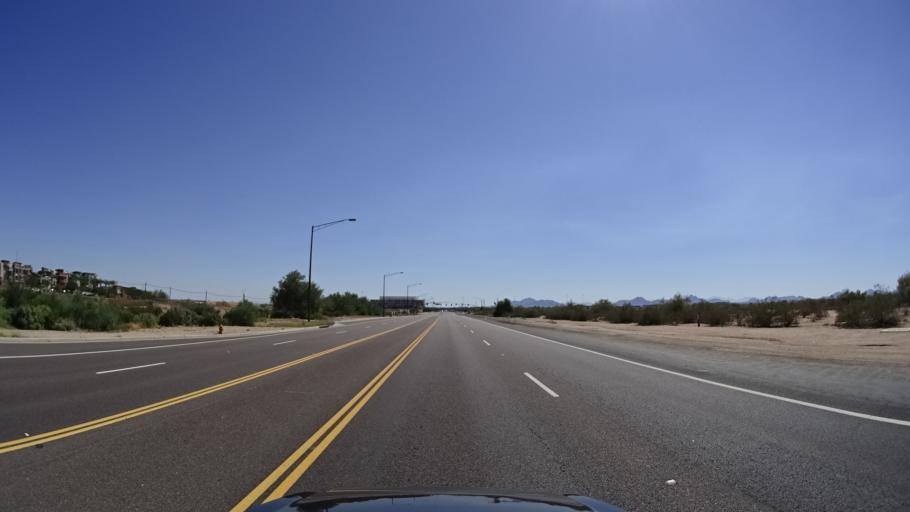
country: US
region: Arizona
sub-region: Maricopa County
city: Paradise Valley
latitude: 33.6669
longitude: -111.9253
